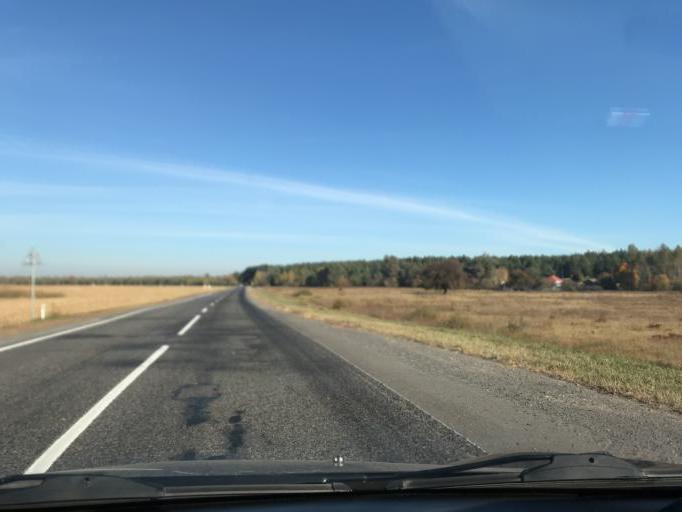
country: UA
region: Chernihiv
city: Lyubech
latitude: 51.5640
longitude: 30.4953
